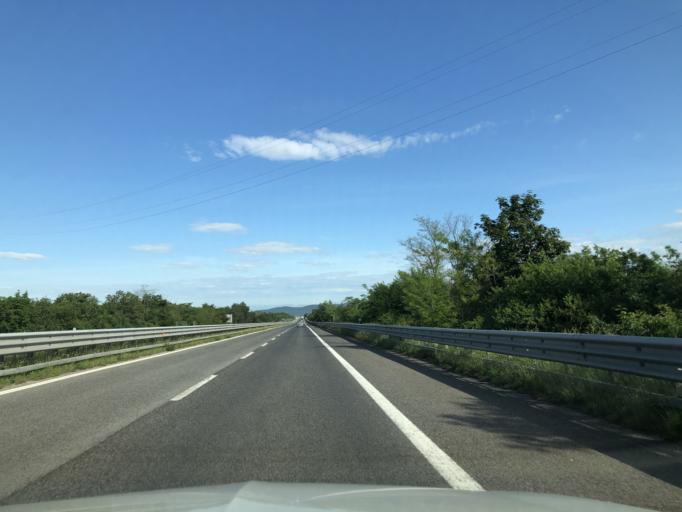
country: IT
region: Friuli Venezia Giulia
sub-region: Provincia di Trieste
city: Prosecco-Contovello
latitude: 45.7264
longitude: 13.7172
